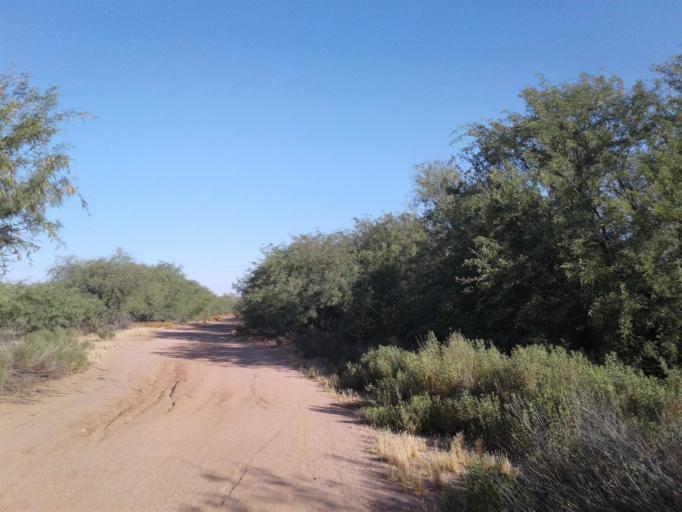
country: US
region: Arizona
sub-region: Maricopa County
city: Paradise Valley
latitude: 33.6673
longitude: -112.0037
